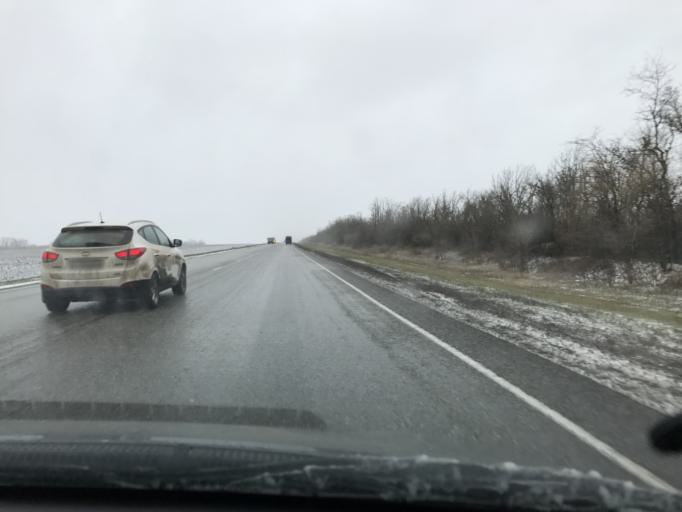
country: RU
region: Rostov
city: Mechetinskaya
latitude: 46.7051
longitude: 40.5010
